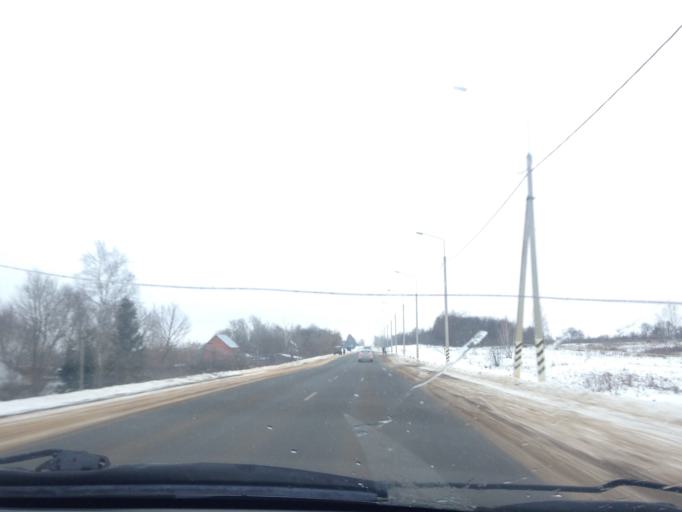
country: RU
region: Tula
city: Shchekino
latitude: 53.9755
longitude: 37.4999
